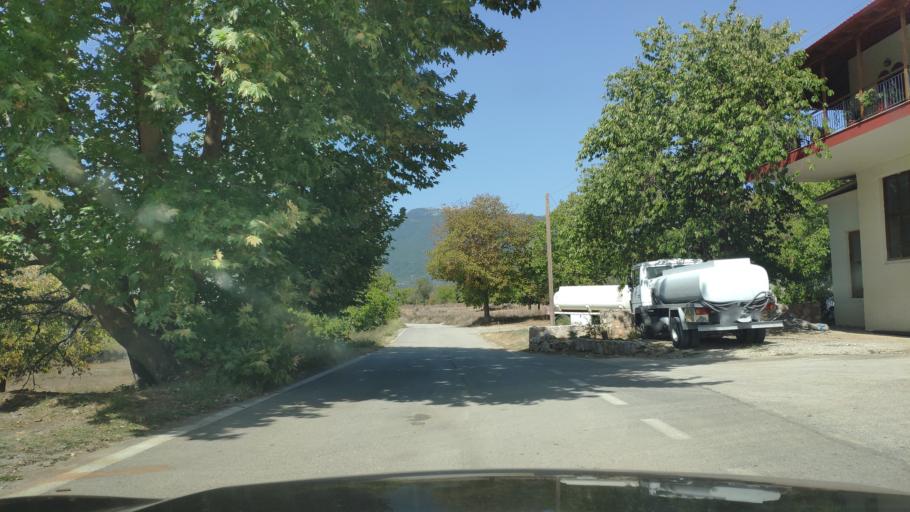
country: GR
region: West Greece
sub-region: Nomos Achaias
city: Aiyira
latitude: 37.9106
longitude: 22.3308
